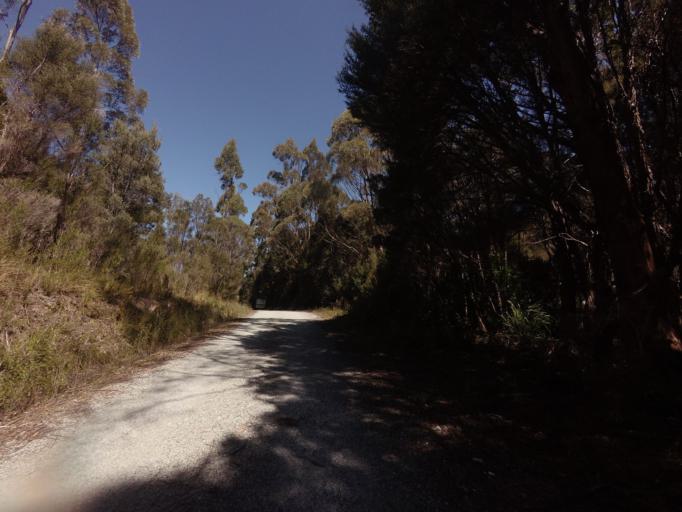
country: AU
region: Tasmania
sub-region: West Coast
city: Queenstown
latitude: -42.7682
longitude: 145.9865
